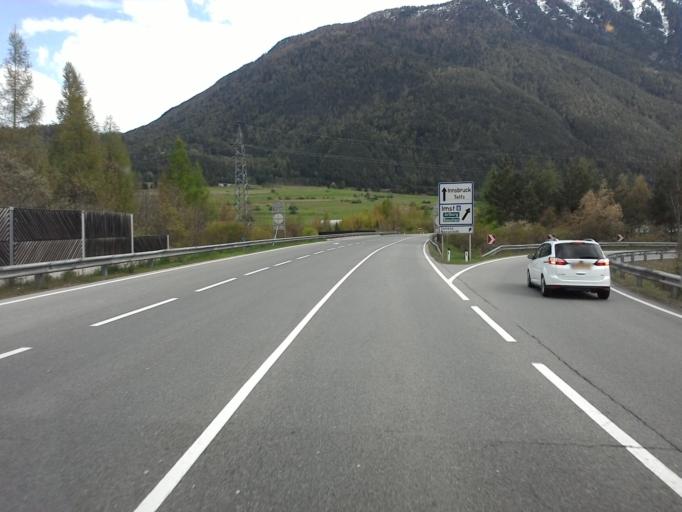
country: AT
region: Tyrol
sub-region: Politischer Bezirk Imst
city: Nassereith
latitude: 47.3058
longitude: 10.8399
